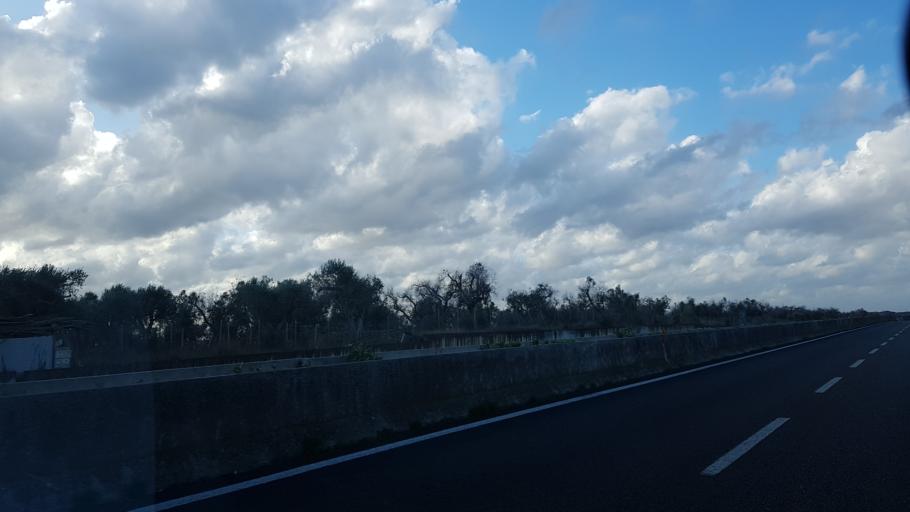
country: IT
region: Apulia
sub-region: Provincia di Lecce
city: Squinzano
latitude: 40.4469
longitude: 18.0722
